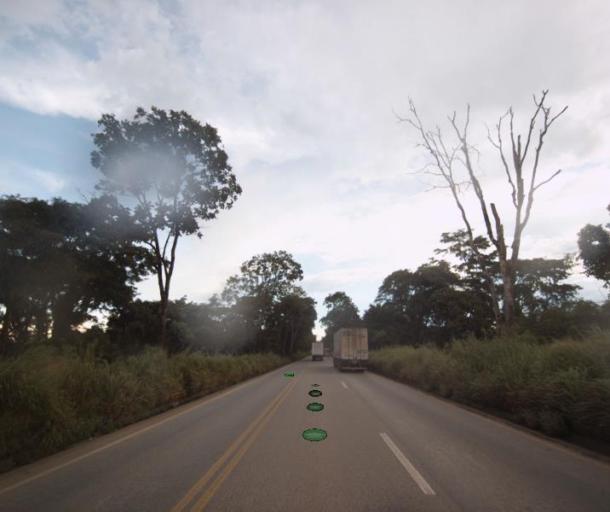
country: BR
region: Goias
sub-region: Porangatu
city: Porangatu
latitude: -13.9716
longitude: -49.0904
